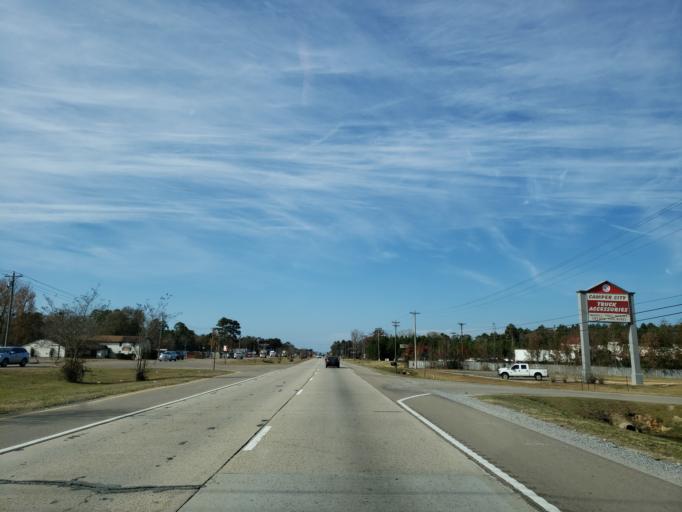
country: US
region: Mississippi
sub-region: Forrest County
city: Rawls Springs
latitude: 31.3841
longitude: -89.3706
